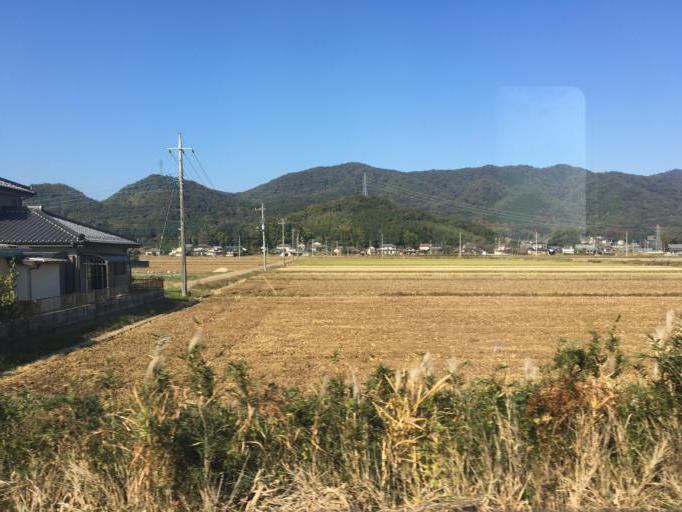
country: JP
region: Tochigi
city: Tochigi
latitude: 36.3332
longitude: 139.6718
